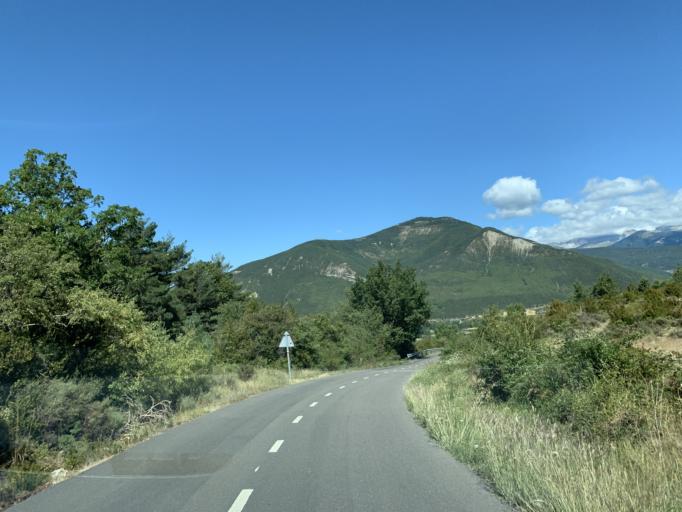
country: ES
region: Aragon
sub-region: Provincia de Huesca
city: Sabinanigo
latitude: 42.5451
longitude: -0.3167
